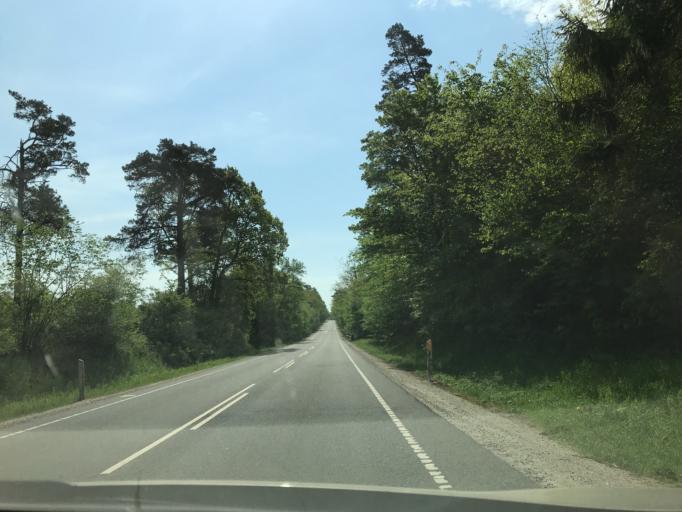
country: DK
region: South Denmark
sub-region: Middelfart Kommune
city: Ejby
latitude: 55.3976
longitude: 9.9045
